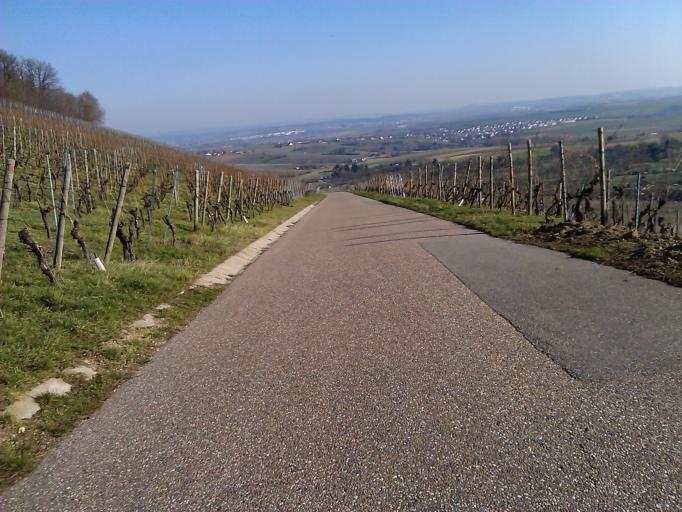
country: DE
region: Baden-Wuerttemberg
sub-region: Regierungsbezirk Stuttgart
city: Leingarten
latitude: 49.1232
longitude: 9.0942
